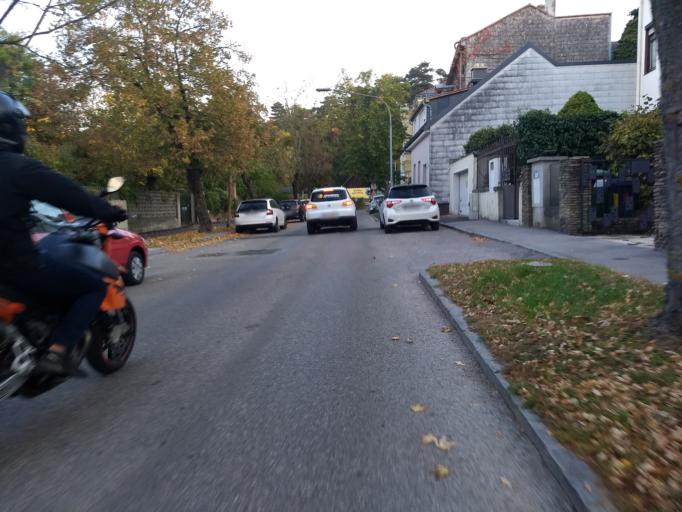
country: AT
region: Lower Austria
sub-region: Politischer Bezirk Modling
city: Perchtoldsdorf
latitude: 48.1227
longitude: 16.2593
